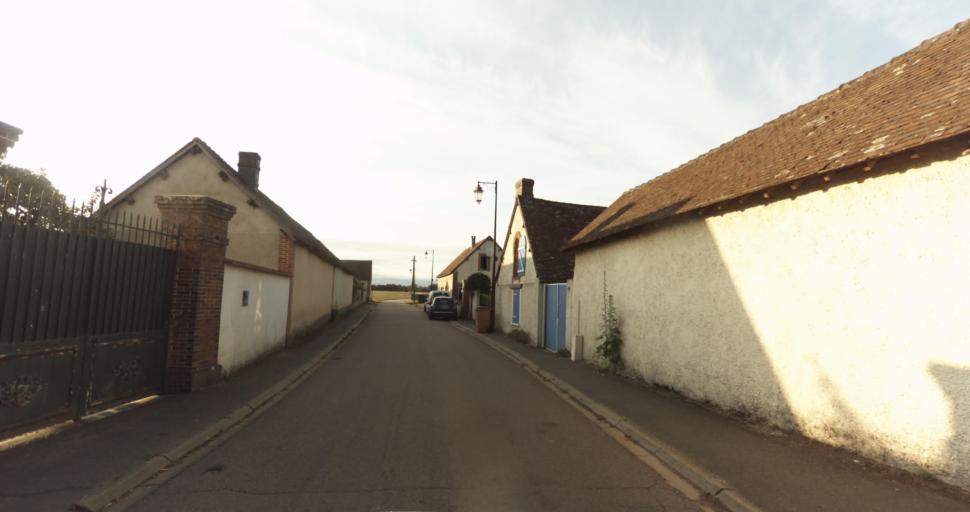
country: FR
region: Haute-Normandie
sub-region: Departement de l'Eure
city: Saint-Germain-sur-Avre
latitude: 48.8221
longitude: 1.2667
